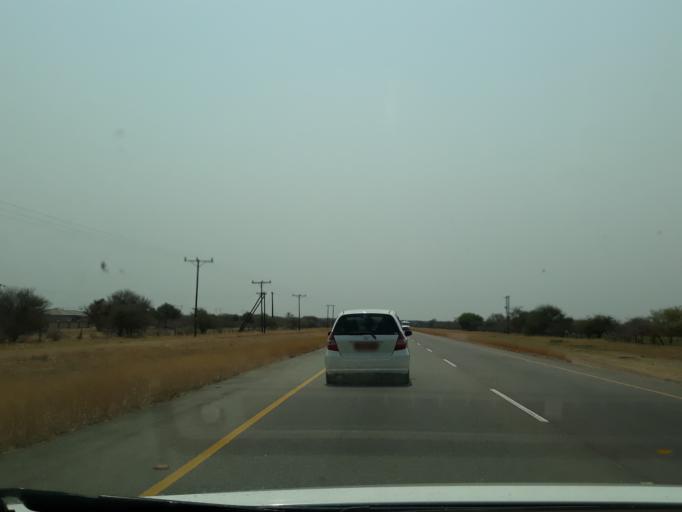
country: BW
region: Kgatleng
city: Mochudi
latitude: -24.3050
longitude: 26.1227
